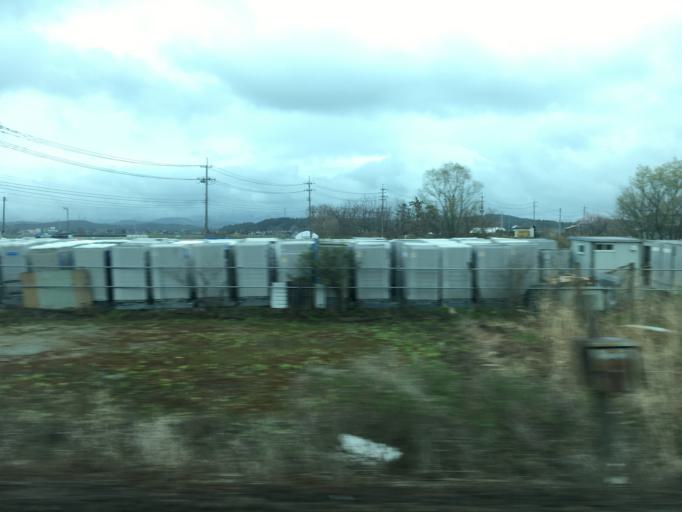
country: JP
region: Akita
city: Akita Shi
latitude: 39.7912
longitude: 140.0644
